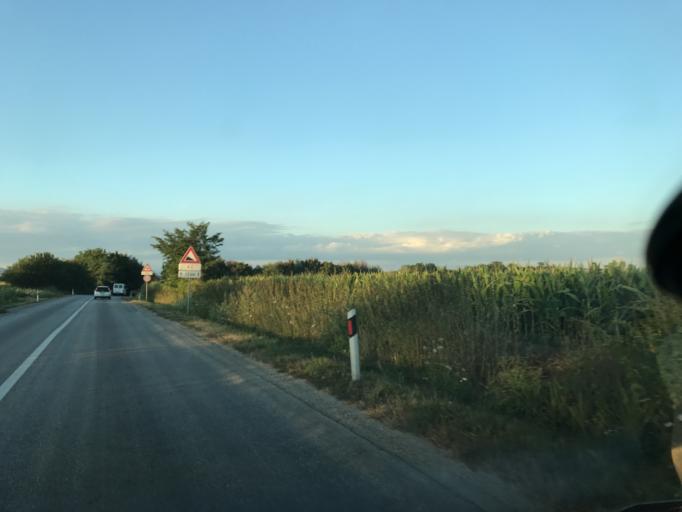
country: RS
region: Central Serbia
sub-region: Branicevski Okrug
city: Veliko Gradiste
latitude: 44.6924
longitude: 21.3738
